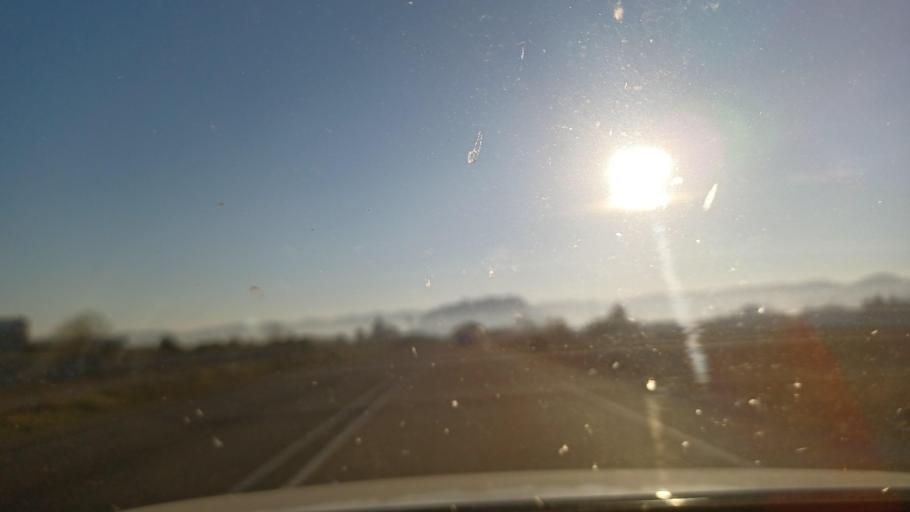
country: ES
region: Valencia
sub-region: Provincia de Valencia
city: Llosa de Ranes
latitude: 39.0140
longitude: -0.5387
